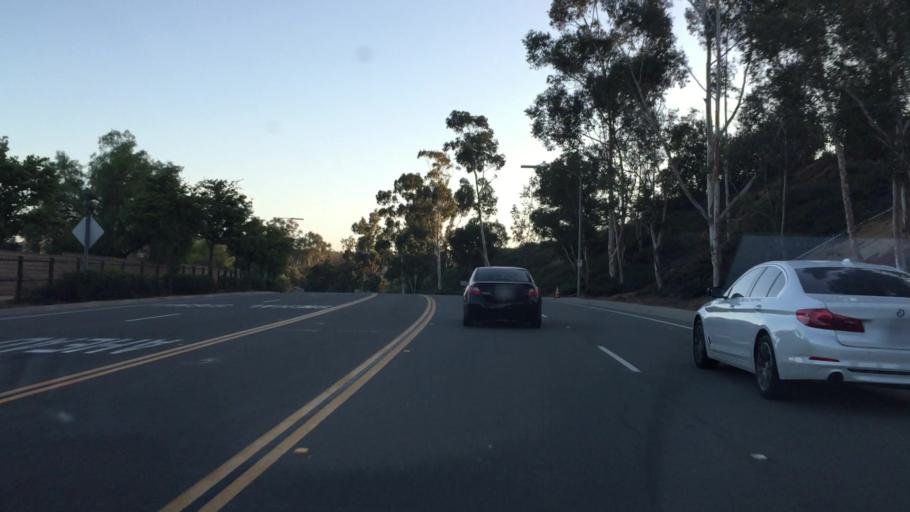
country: US
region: California
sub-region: San Diego County
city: Poway
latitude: 32.9777
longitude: -117.0381
